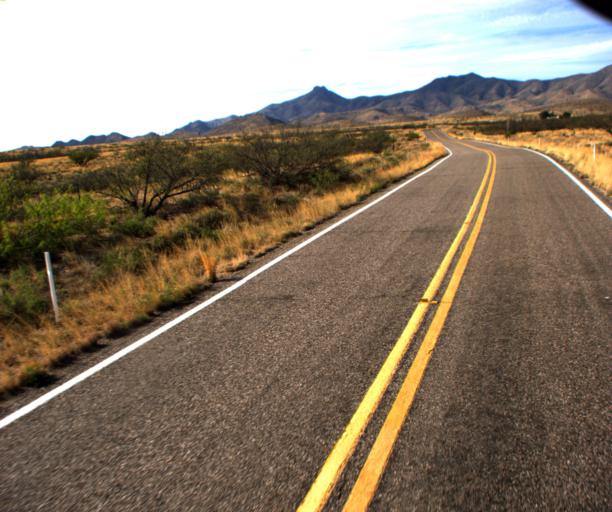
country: US
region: Arizona
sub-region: Cochise County
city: Willcox
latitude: 32.1247
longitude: -109.5560
